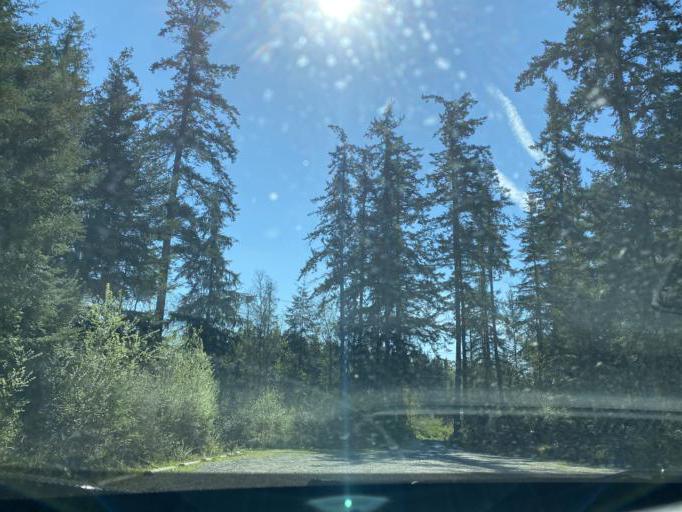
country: US
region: Washington
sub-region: Island County
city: Freeland
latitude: 48.0503
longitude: -122.5681
